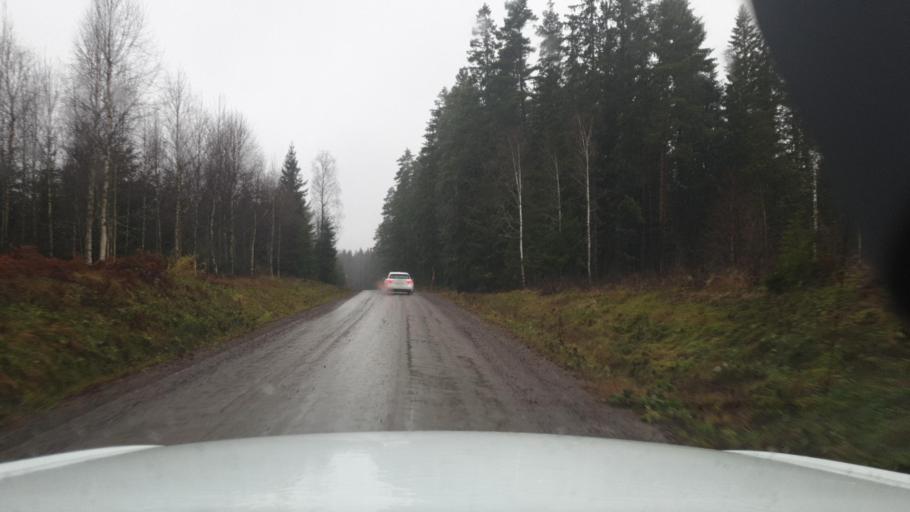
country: SE
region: Vaermland
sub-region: Sunne Kommun
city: Sunne
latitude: 59.8053
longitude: 13.0810
